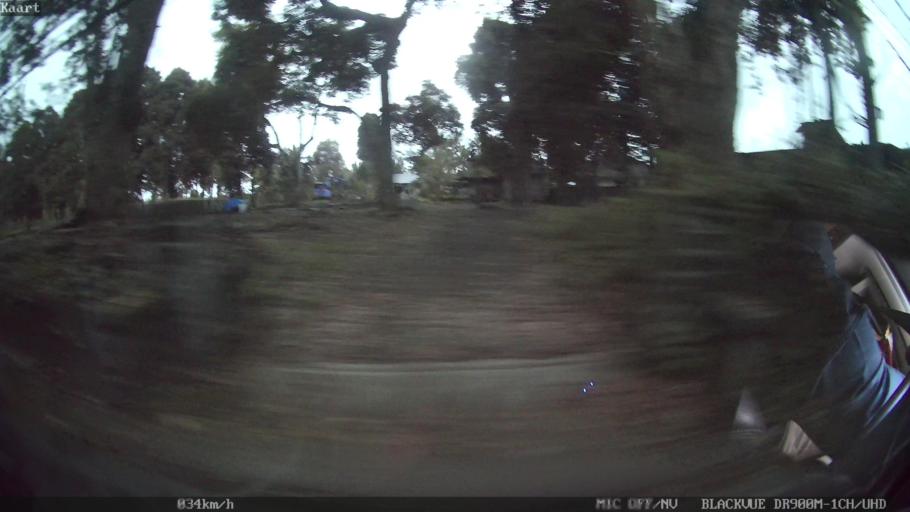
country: ID
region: Bali
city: Banjar Buahan
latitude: -8.4139
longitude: 115.2441
